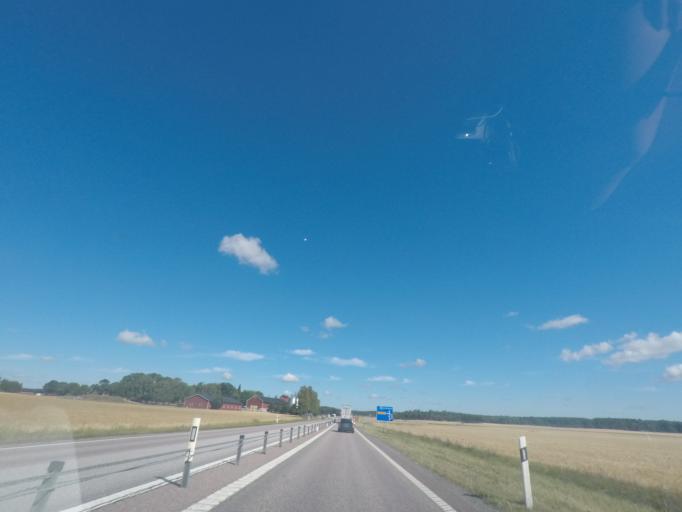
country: SE
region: Uppsala
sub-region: Enkopings Kommun
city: Orsundsbro
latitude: 59.6953
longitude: 17.2789
